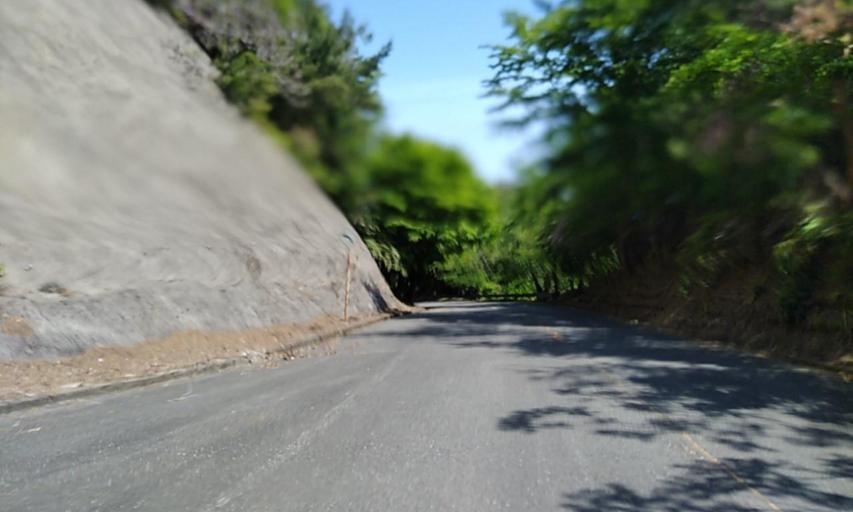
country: JP
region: Fukui
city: Obama
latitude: 35.5459
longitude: 135.7383
